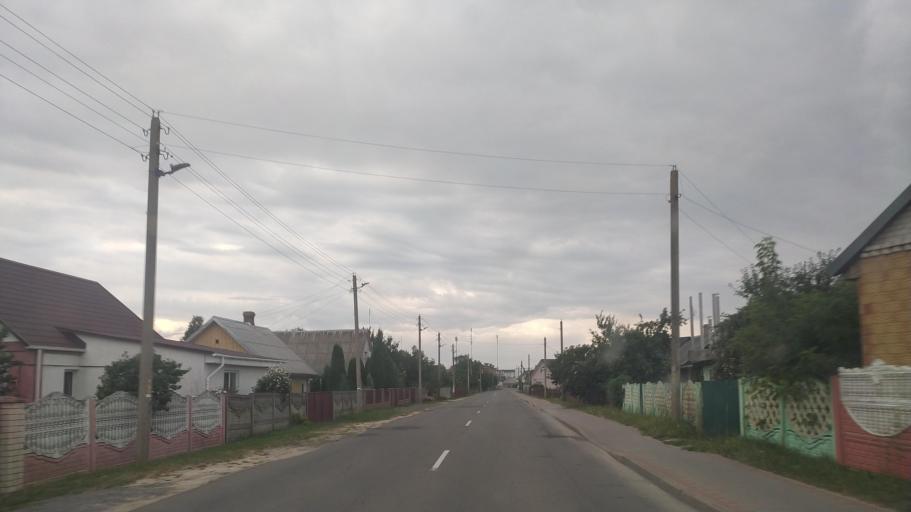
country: BY
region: Brest
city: Byaroza
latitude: 52.5247
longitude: 24.9739
